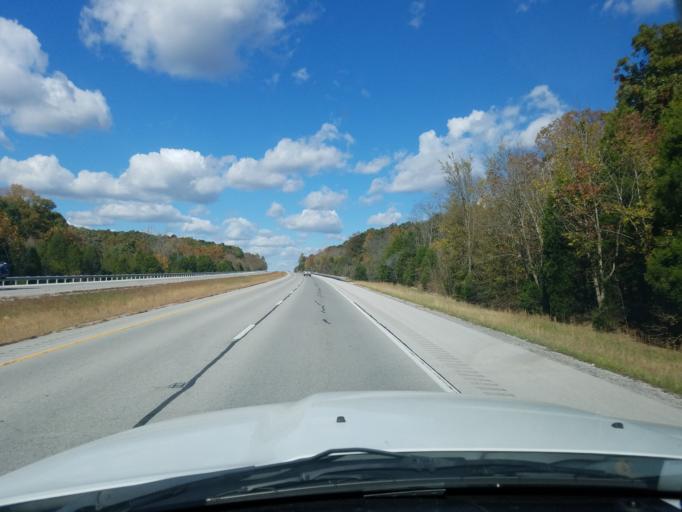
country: US
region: Kentucky
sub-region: Butler County
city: Morgantown
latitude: 37.0926
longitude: -86.6285
